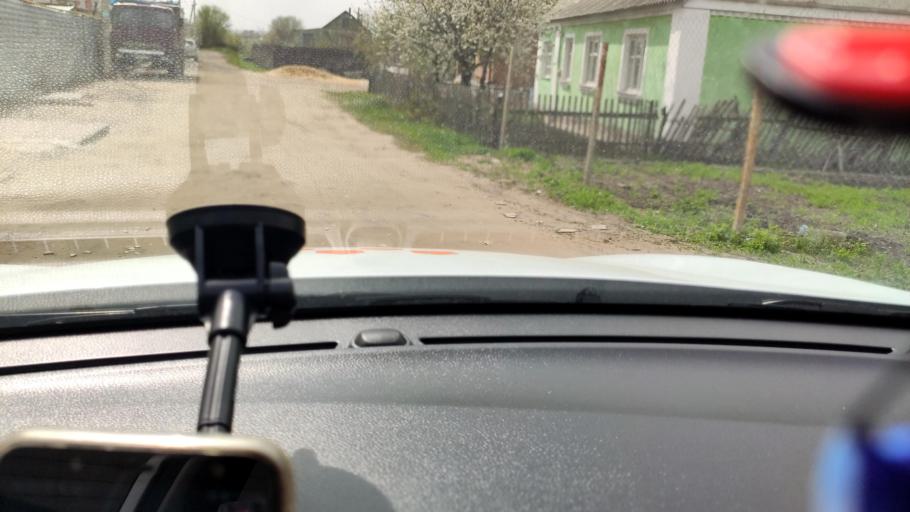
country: RU
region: Voronezj
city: Pridonskoy
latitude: 51.6608
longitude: 39.0906
